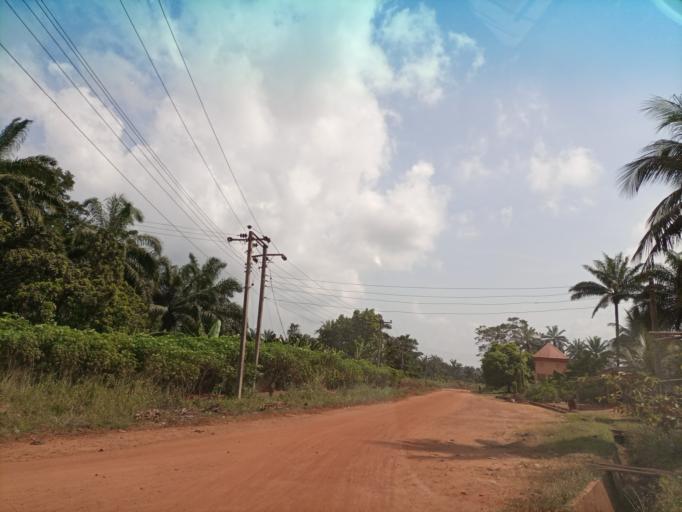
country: NG
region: Enugu
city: Oji River
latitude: 6.3116
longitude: 7.3100
